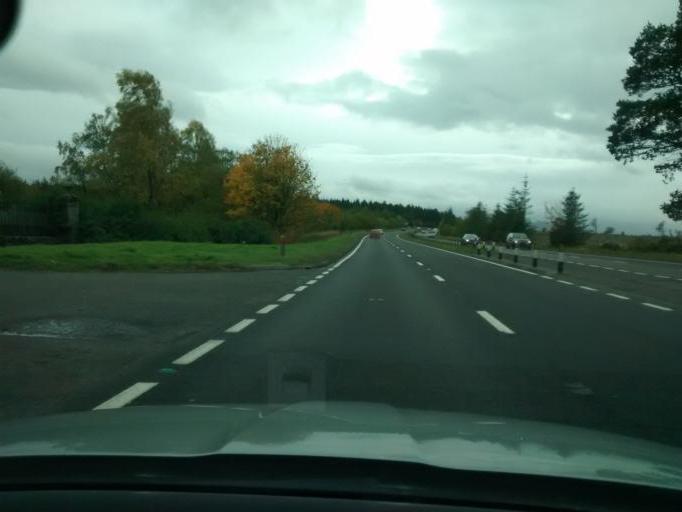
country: GB
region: Scotland
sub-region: Perth and Kinross
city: Methven
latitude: 56.3628
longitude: -3.5563
